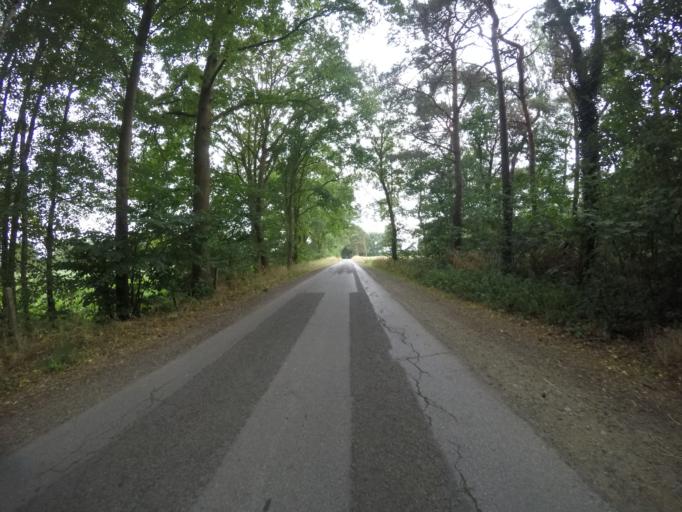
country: DE
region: North Rhine-Westphalia
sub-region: Regierungsbezirk Dusseldorf
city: Bocholt
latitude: 51.7831
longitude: 6.6294
